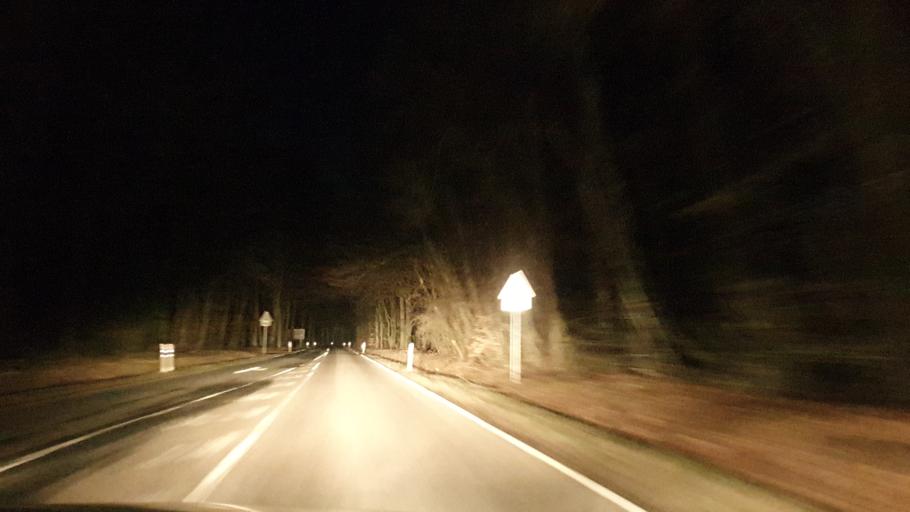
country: DE
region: Rheinland-Pfalz
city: Oberdreis
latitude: 50.6319
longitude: 7.6537
